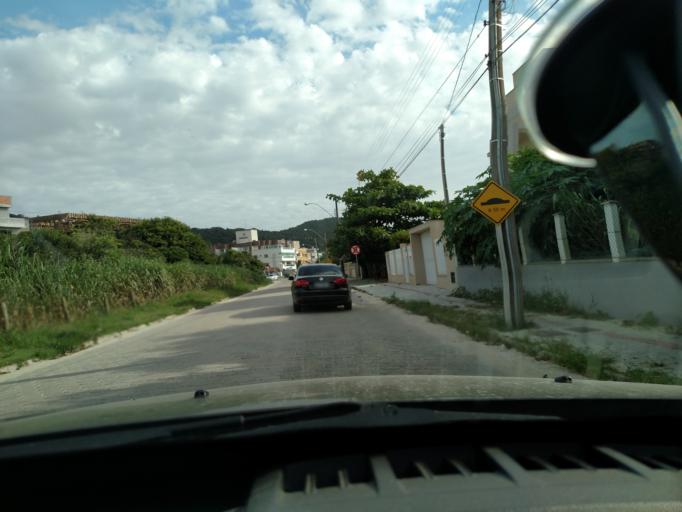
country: BR
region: Santa Catarina
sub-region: Porto Belo
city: Porto Belo
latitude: -27.1746
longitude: -48.5004
